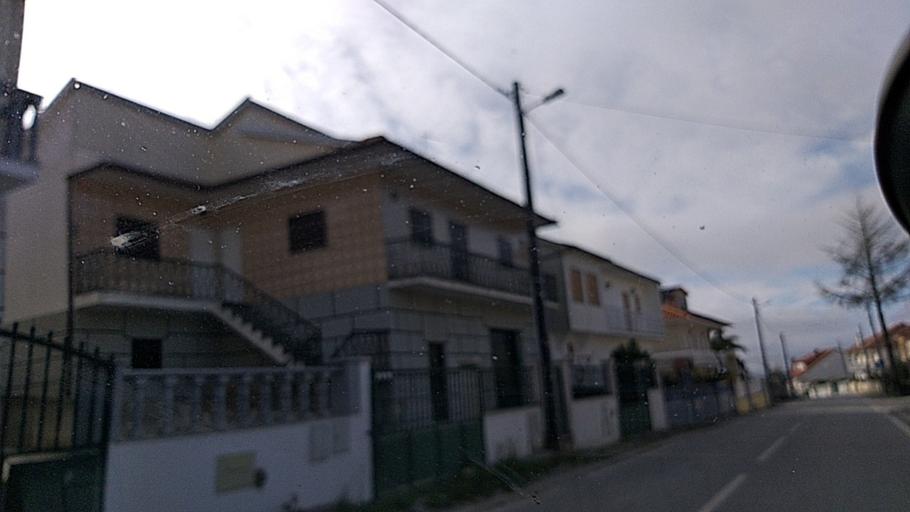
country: PT
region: Guarda
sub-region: Aguiar da Beira
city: Aguiar da Beira
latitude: 40.7812
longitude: -7.5180
